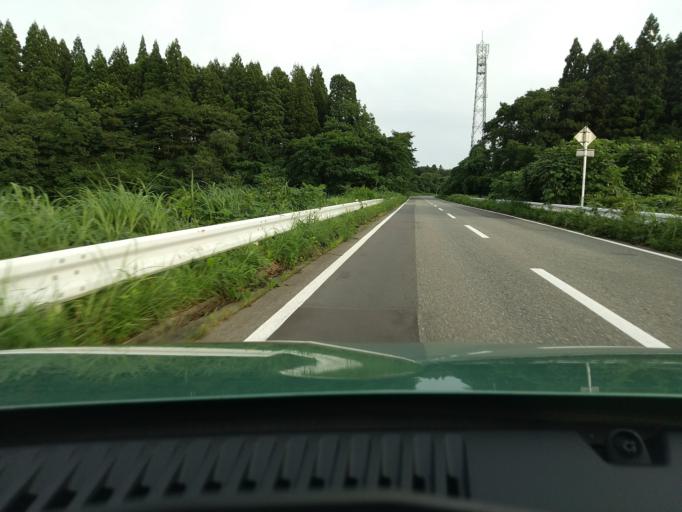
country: JP
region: Akita
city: Akita
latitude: 39.7603
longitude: 140.1597
